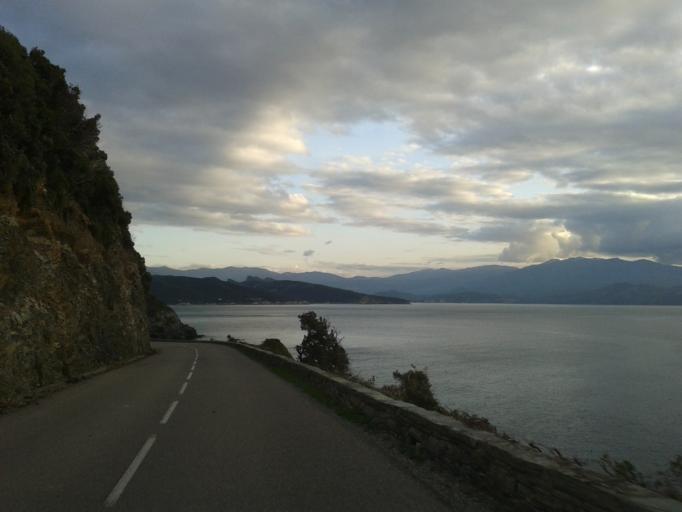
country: FR
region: Corsica
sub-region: Departement de la Haute-Corse
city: Saint-Florent
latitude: 42.7644
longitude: 9.3378
